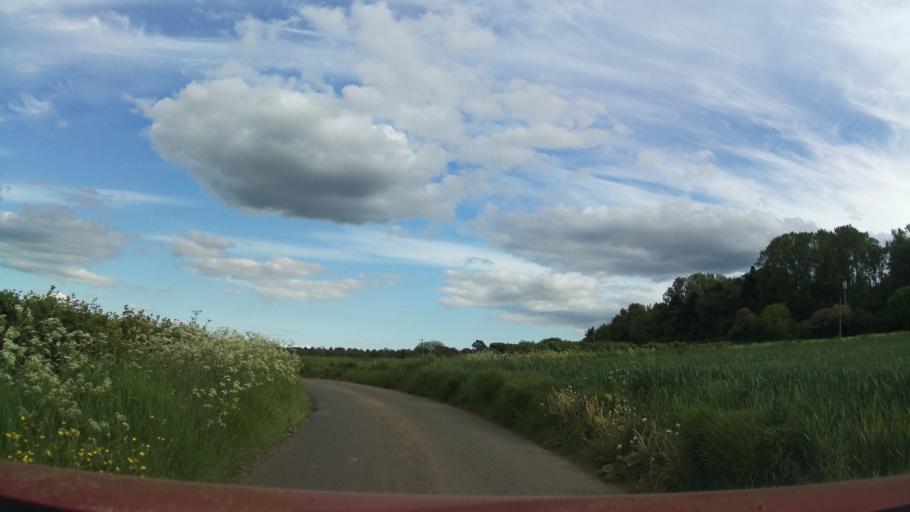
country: GB
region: England
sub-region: Gloucestershire
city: Moreton in Marsh
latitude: 52.0244
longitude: -1.7128
